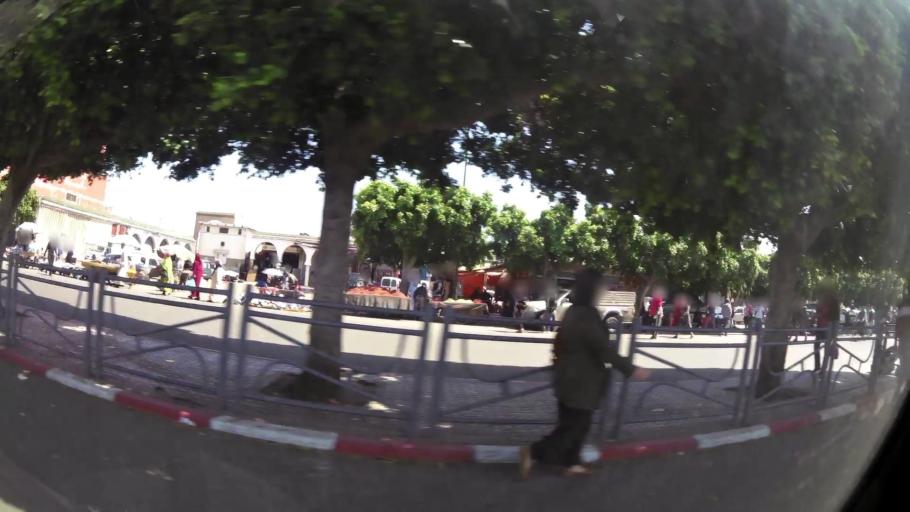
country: MA
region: Souss-Massa-Draa
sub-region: Inezgane-Ait Mellou
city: Inezgane
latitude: 30.3590
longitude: -9.5302
